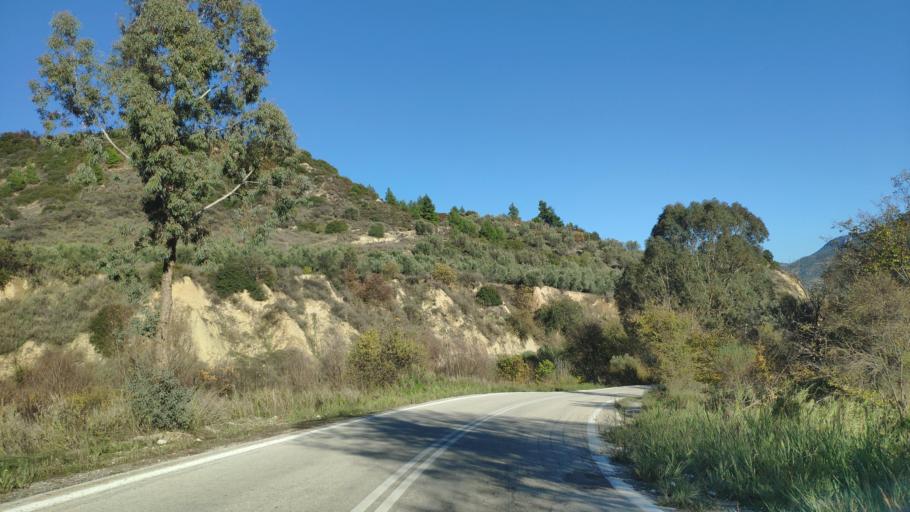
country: GR
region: Peloponnese
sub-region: Nomos Korinthias
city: Xylokastro
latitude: 38.0089
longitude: 22.5199
